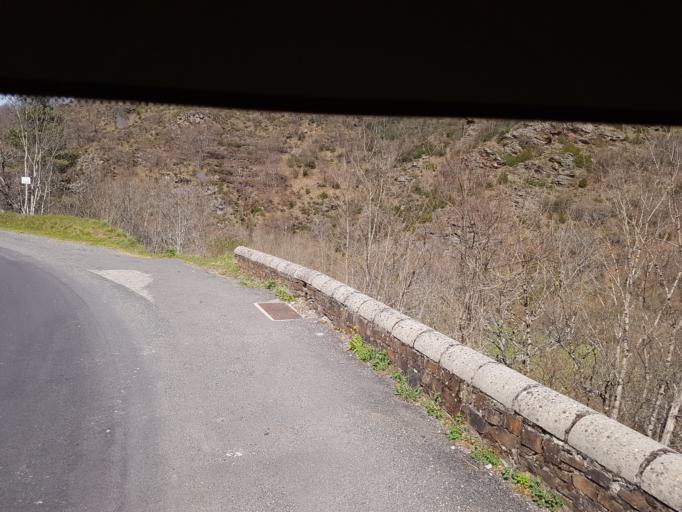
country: FR
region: Languedoc-Roussillon
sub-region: Departement de la Lozere
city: Florac
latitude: 44.2454
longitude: 3.5842
